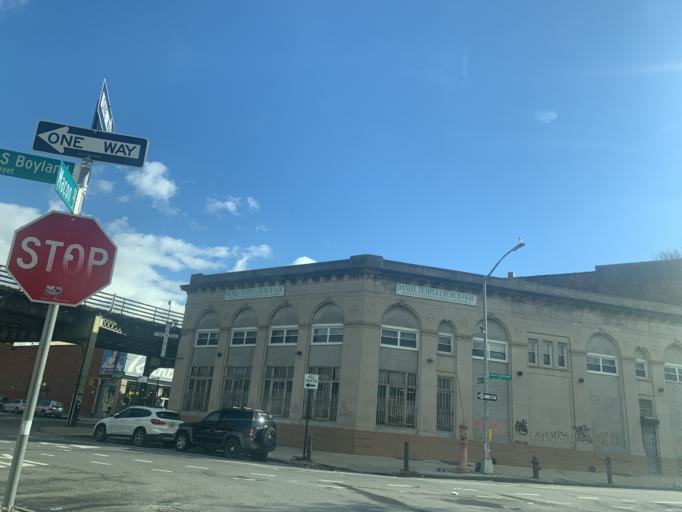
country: US
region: New York
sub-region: Kings County
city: East New York
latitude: 40.6851
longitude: -73.9151
